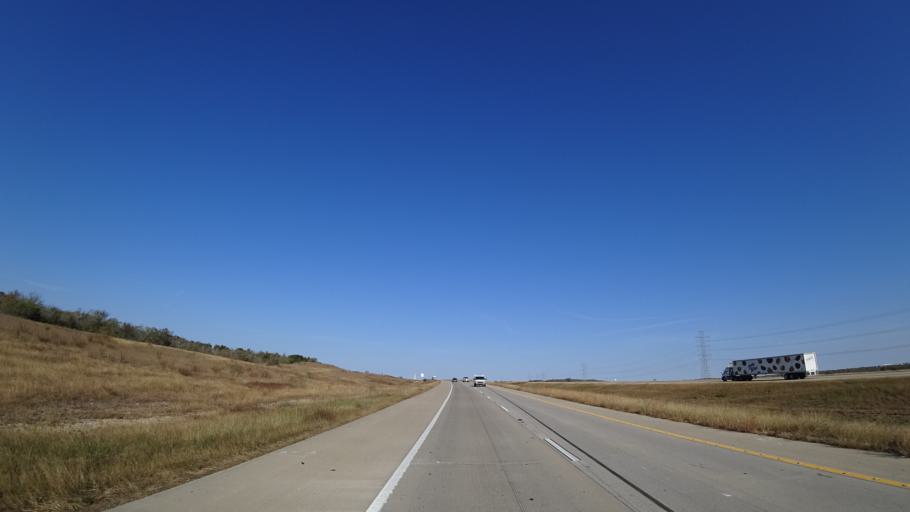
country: US
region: Texas
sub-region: Travis County
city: Manor
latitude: 30.3122
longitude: -97.5717
